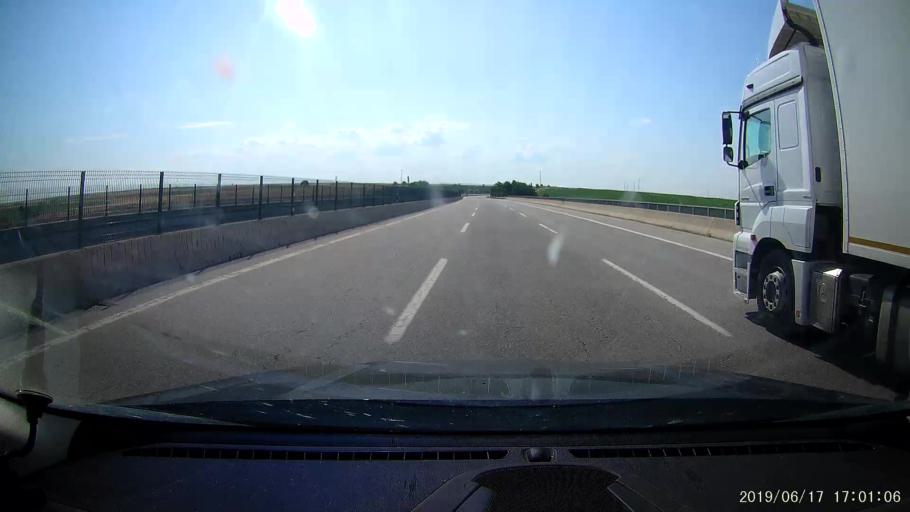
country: TR
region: Edirne
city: Haskoy
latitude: 41.6268
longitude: 26.8130
